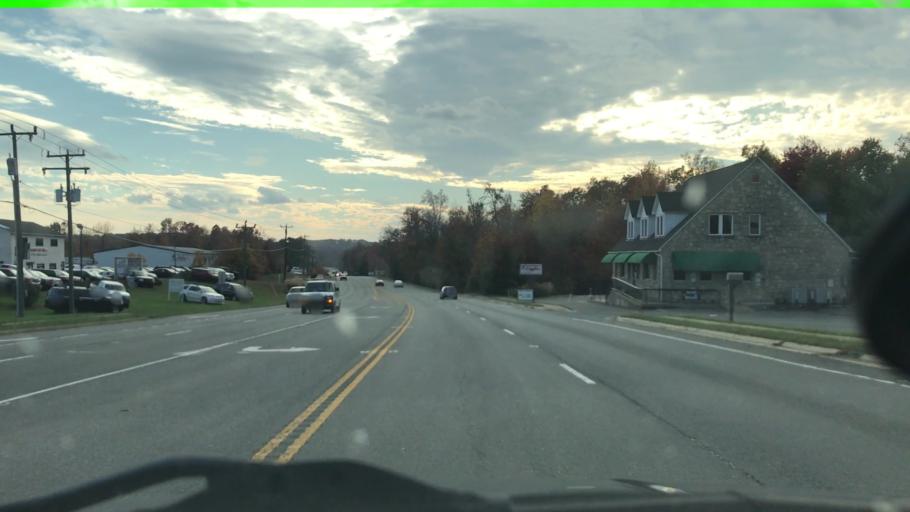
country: US
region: Virginia
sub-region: Stafford County
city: Stafford
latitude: 38.3849
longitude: -77.4433
